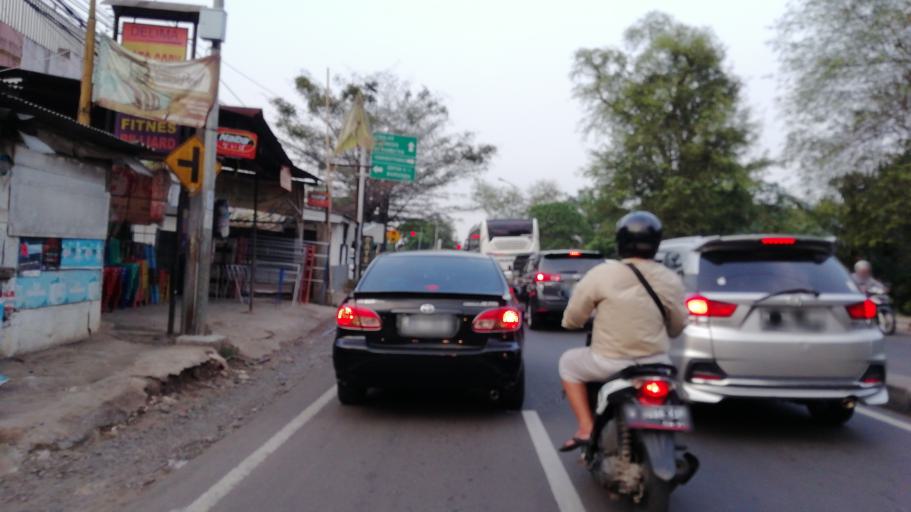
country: ID
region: West Java
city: Depok
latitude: -6.4117
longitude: 106.8610
